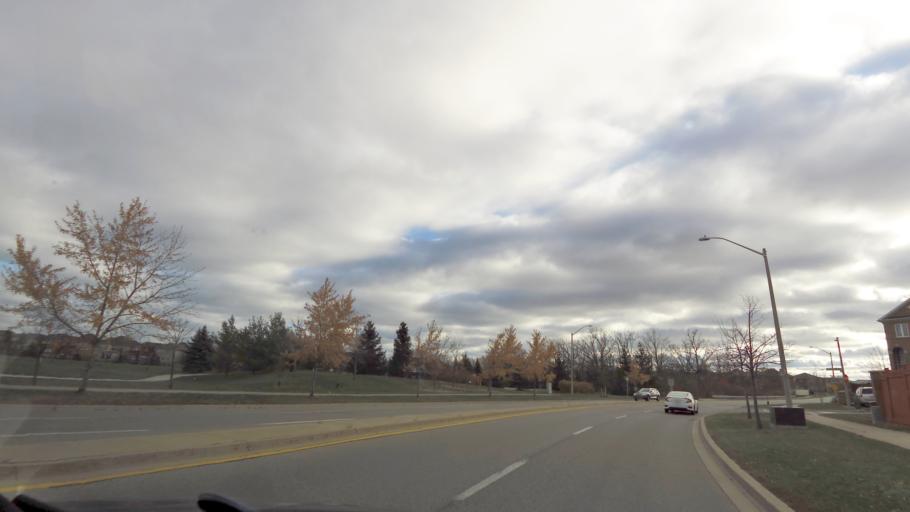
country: CA
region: Ontario
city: Oakville
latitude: 43.4877
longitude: -79.7130
